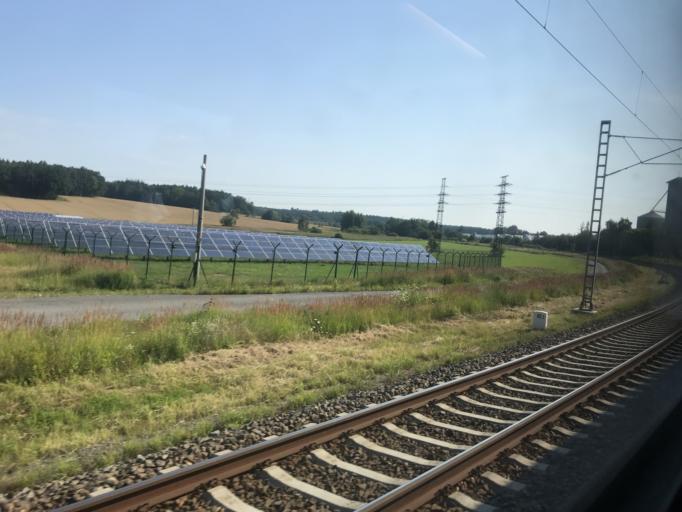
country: CZ
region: Jihocesky
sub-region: Okres Tabor
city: Tabor
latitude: 49.4318
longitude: 14.6799
